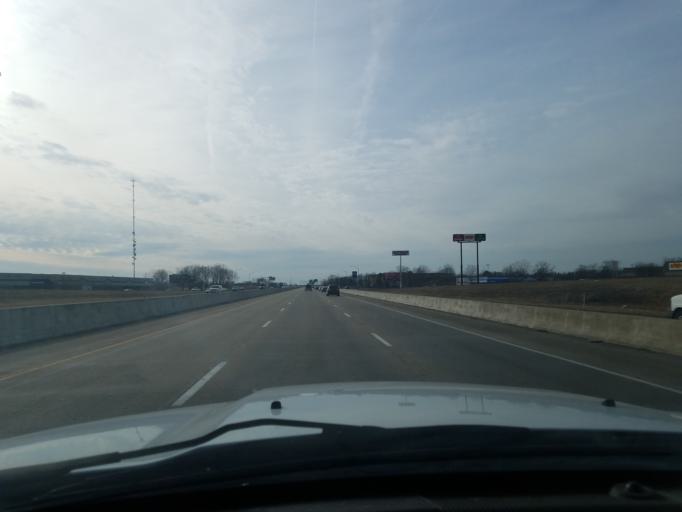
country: US
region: Indiana
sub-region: Marion County
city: Lawrence
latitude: 39.8008
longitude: -86.0111
